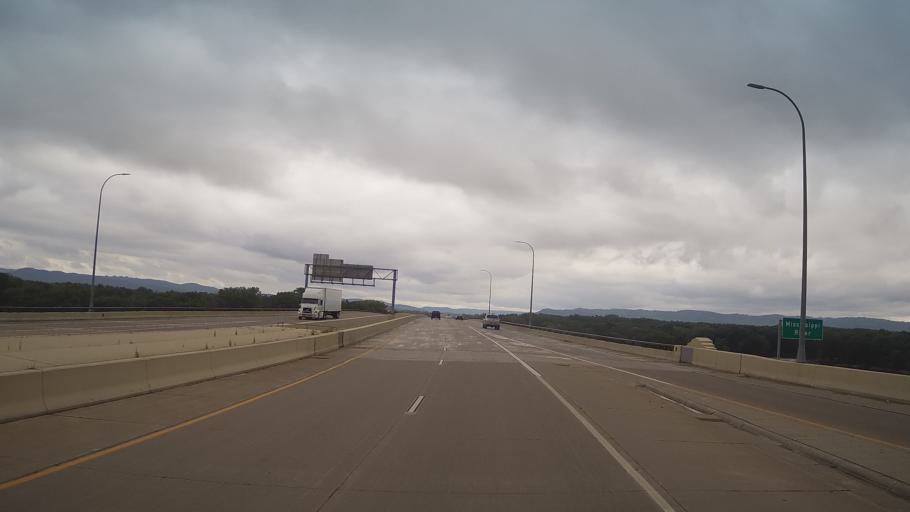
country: US
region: Minnesota
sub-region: Houston County
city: La Crescent
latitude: 43.8577
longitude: -91.3026
